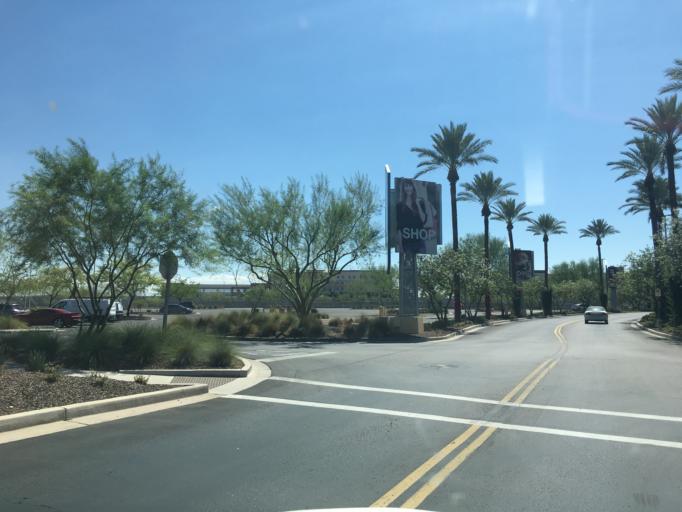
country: US
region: Arizona
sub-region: Maricopa County
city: Tempe
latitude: 33.4313
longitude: -111.9017
